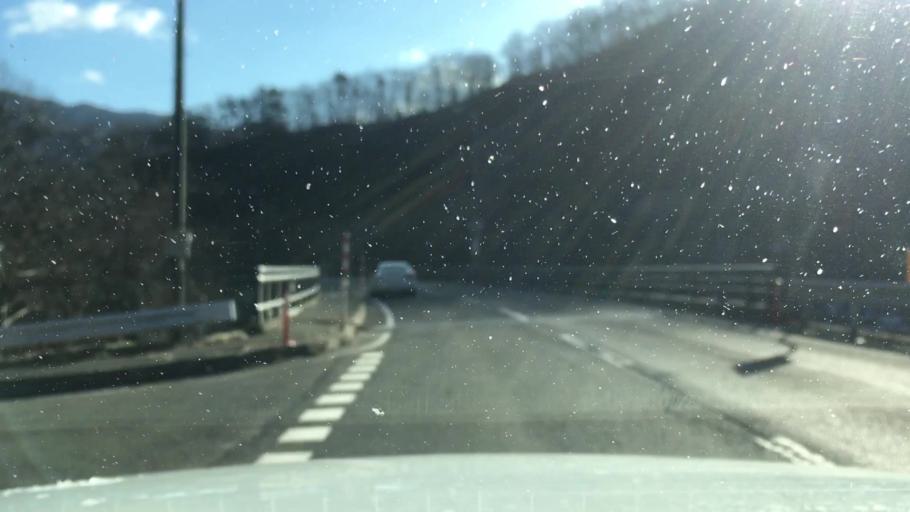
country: JP
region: Iwate
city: Tono
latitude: 39.6482
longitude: 141.5862
